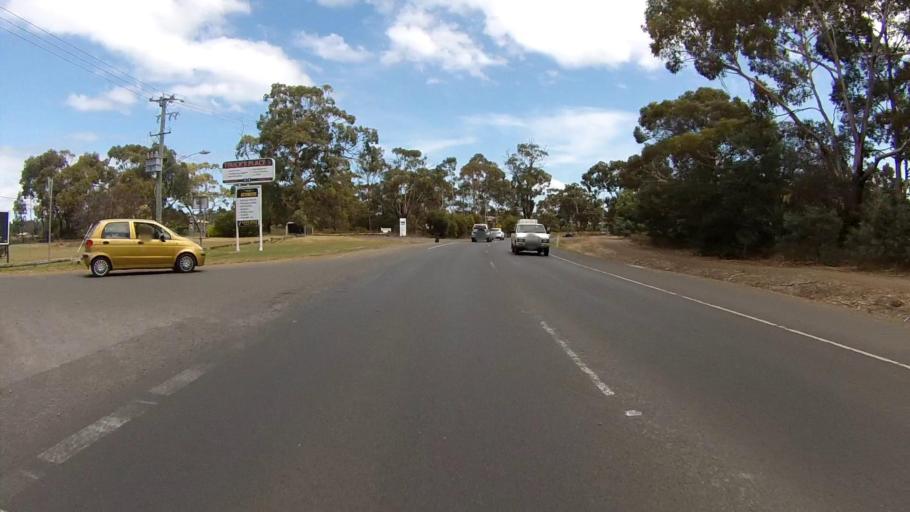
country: AU
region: Tasmania
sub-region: Sorell
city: Sorell
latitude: -42.8492
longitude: 147.6268
